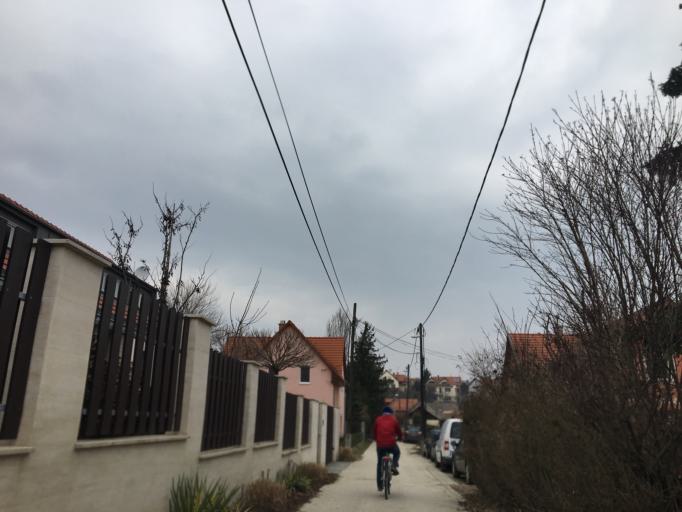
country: HU
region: Pest
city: Budakalasz
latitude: 47.5986
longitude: 19.0402
